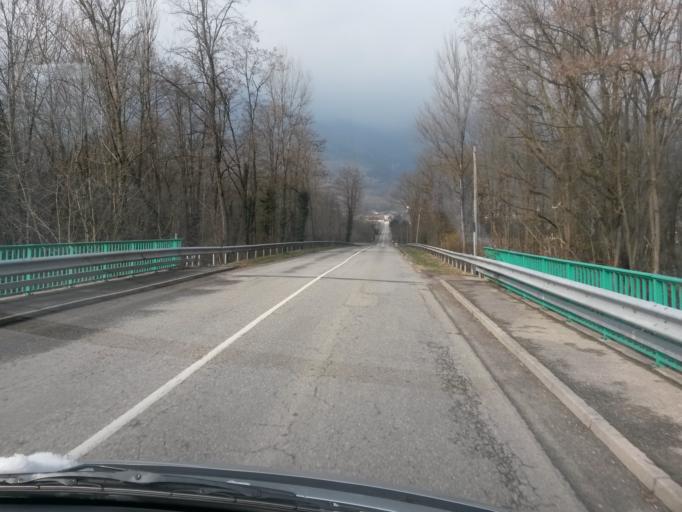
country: FR
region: Rhone-Alpes
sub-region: Departement de l'Isere
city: La Terrasse
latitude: 45.3178
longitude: 5.9421
